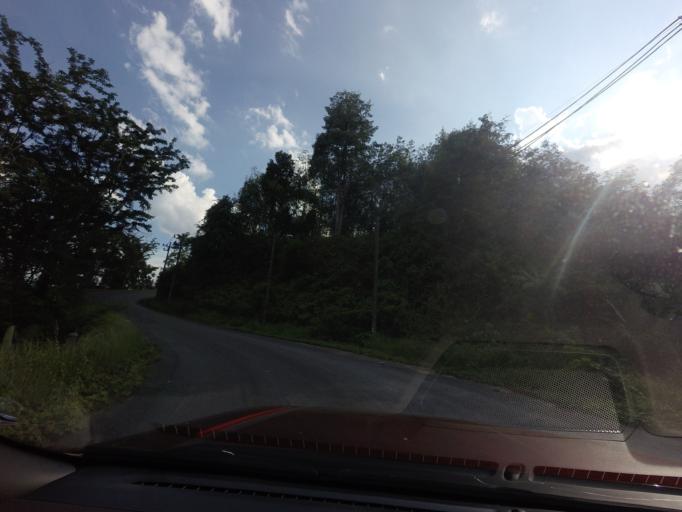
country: TH
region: Yala
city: Than To
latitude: 6.1430
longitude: 101.2883
